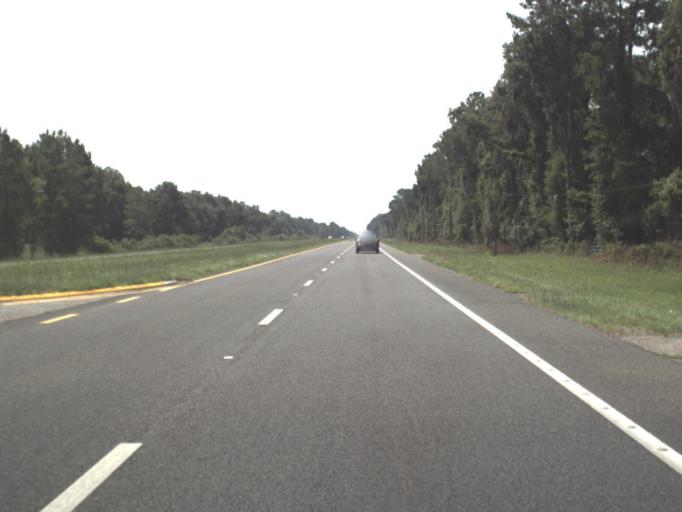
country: US
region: Florida
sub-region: Levy County
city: Chiefland
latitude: 29.4575
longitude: -82.8484
